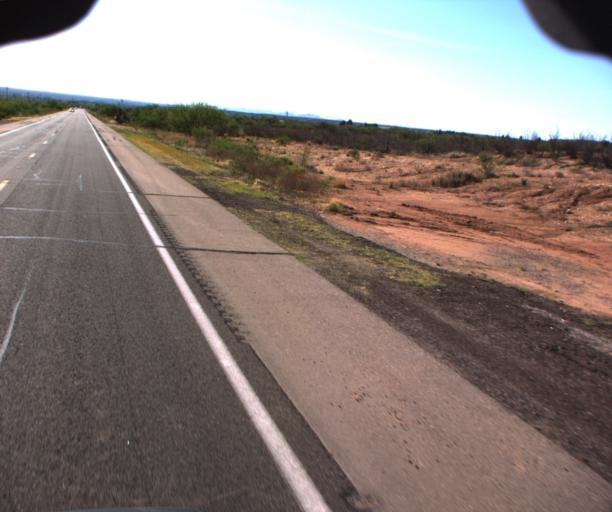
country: US
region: Arizona
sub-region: Cochise County
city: Benson
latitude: 31.9260
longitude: -110.2755
